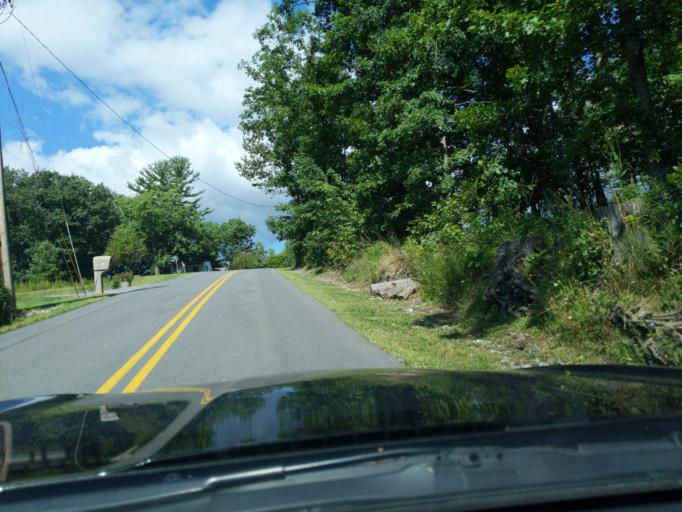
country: US
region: Pennsylvania
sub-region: Blair County
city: Altoona
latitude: 40.5462
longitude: -78.4011
